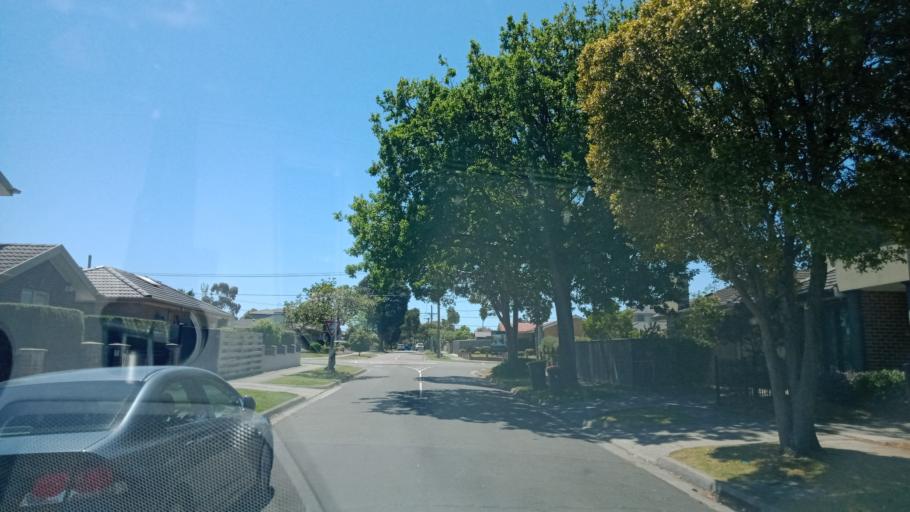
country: AU
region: Victoria
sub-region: Greater Dandenong
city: Springvale
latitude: -37.9306
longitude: 145.1688
